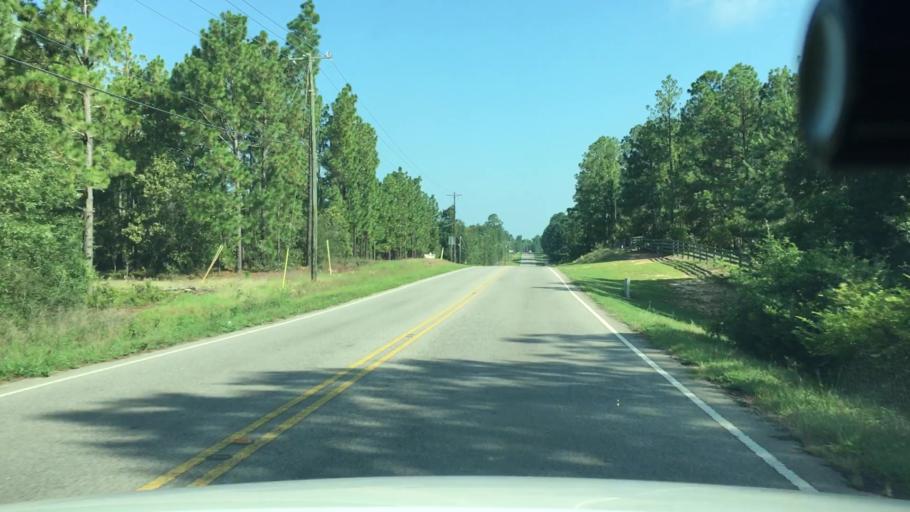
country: US
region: South Carolina
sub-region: Aiken County
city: Graniteville
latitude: 33.5942
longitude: -81.8379
